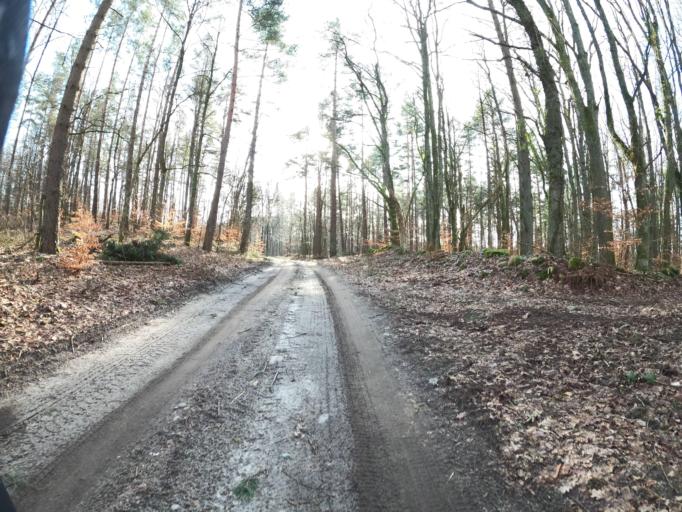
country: PL
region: West Pomeranian Voivodeship
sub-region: Powiat koszalinski
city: Polanow
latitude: 54.2315
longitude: 16.6390
